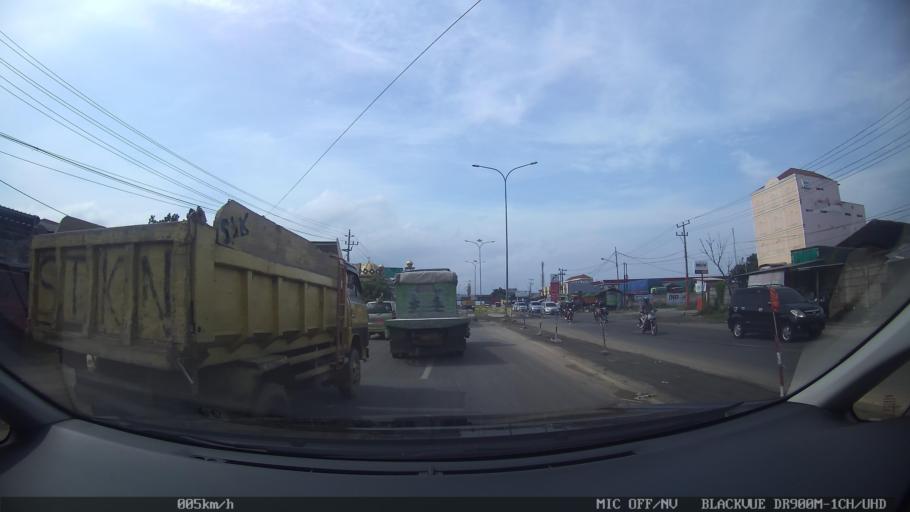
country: ID
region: Lampung
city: Kedaton
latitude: -5.3957
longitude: 105.2894
